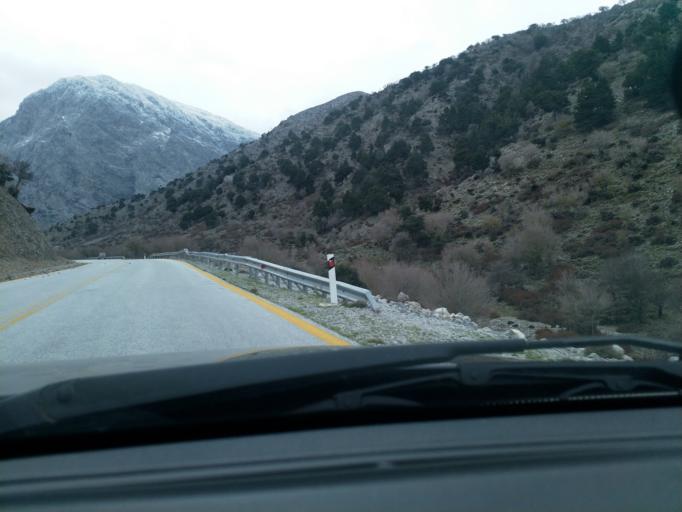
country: GR
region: Crete
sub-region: Nomos Chanias
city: Perivolia
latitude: 35.3147
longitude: 23.9155
